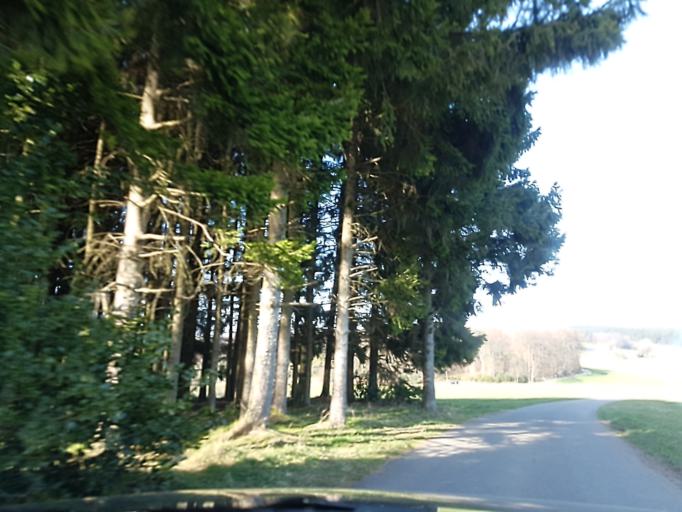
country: DE
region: North Rhine-Westphalia
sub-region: Regierungsbezirk Koln
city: Marienheide
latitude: 51.1154
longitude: 7.5326
